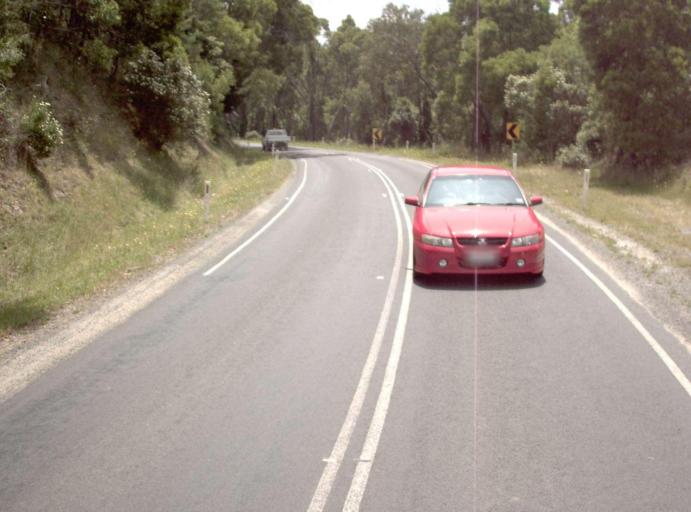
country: AU
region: Victoria
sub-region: Latrobe
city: Traralgon
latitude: -38.3903
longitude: 146.7527
